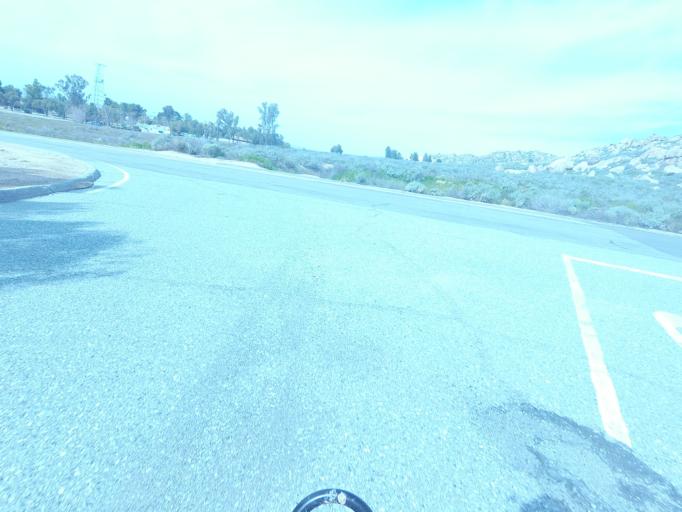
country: US
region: California
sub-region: Riverside County
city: March Air Force Base
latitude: 33.8619
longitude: -117.2005
